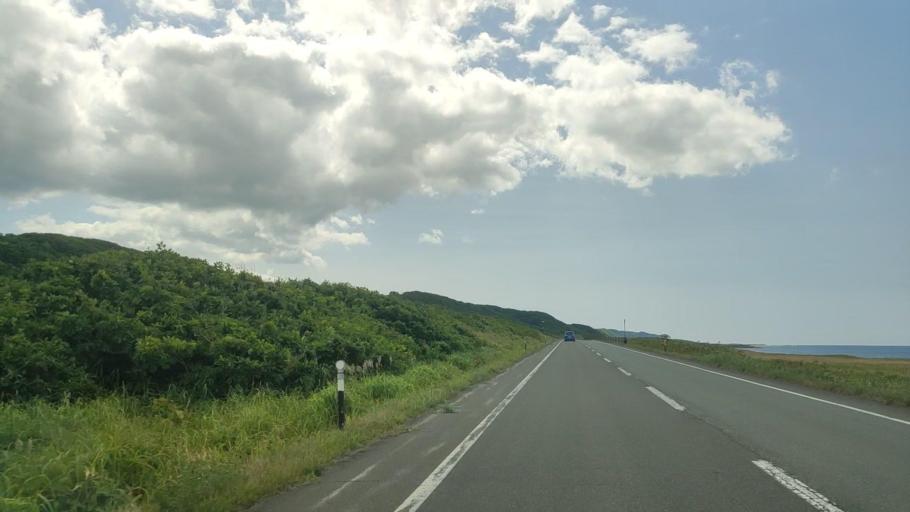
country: JP
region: Hokkaido
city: Wakkanai
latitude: 45.2760
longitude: 141.6142
